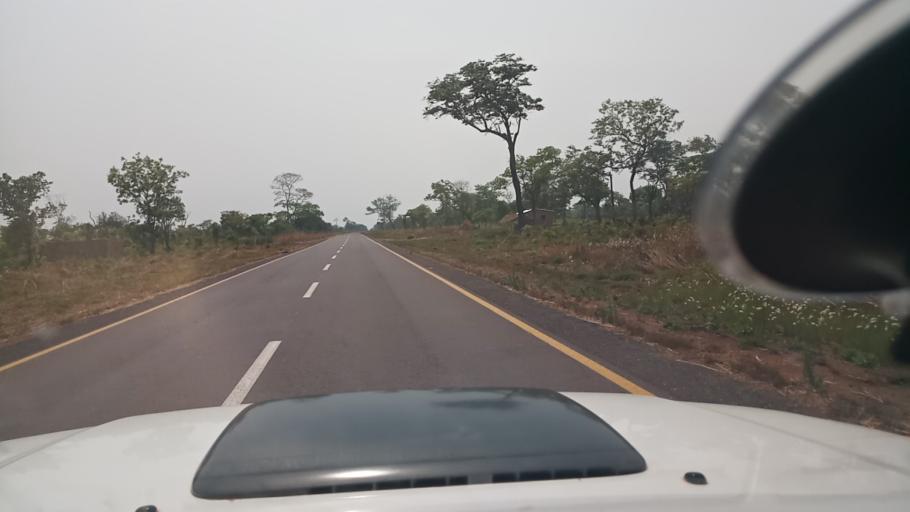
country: ZM
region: Luapula
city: Mansa
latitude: -10.9856
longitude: 28.1226
